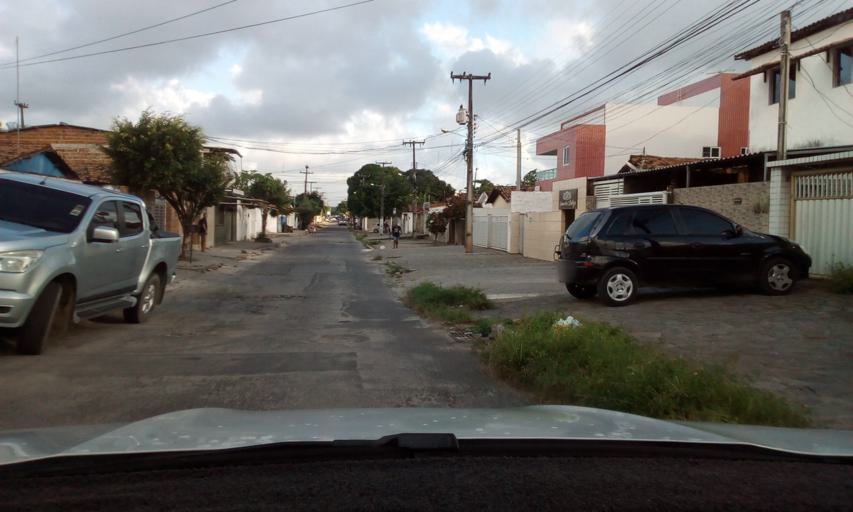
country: BR
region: Paraiba
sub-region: Joao Pessoa
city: Joao Pessoa
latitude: -7.1680
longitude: -34.8366
